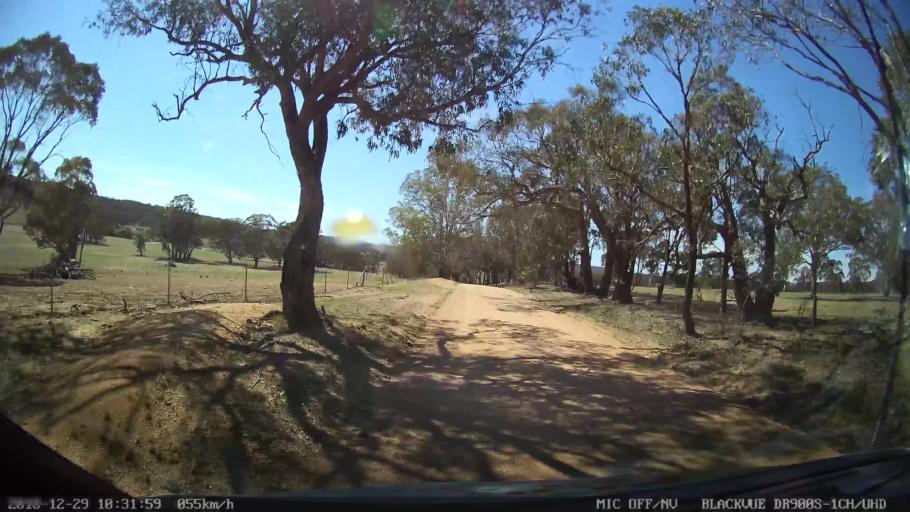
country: AU
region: New South Wales
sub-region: Yass Valley
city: Gundaroo
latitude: -34.9722
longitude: 149.4609
